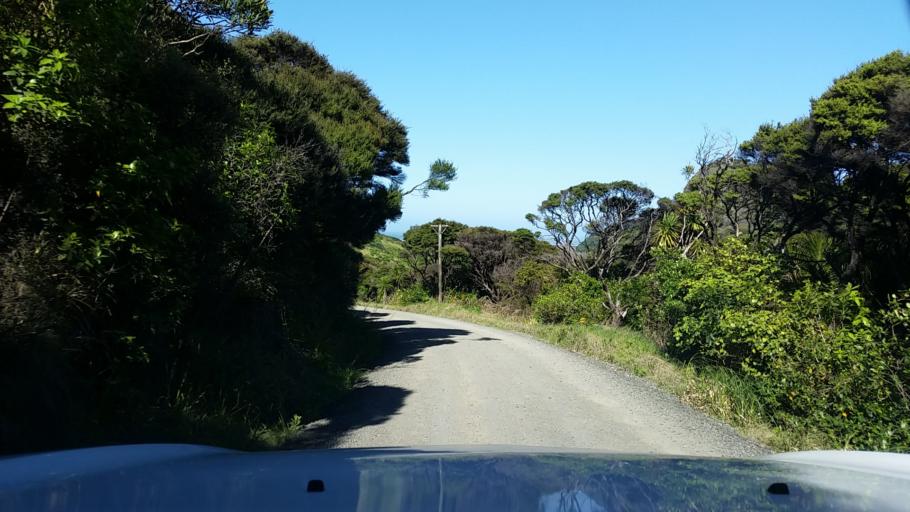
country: NZ
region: Auckland
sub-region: Auckland
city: Titirangi
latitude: -37.0350
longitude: 174.5153
